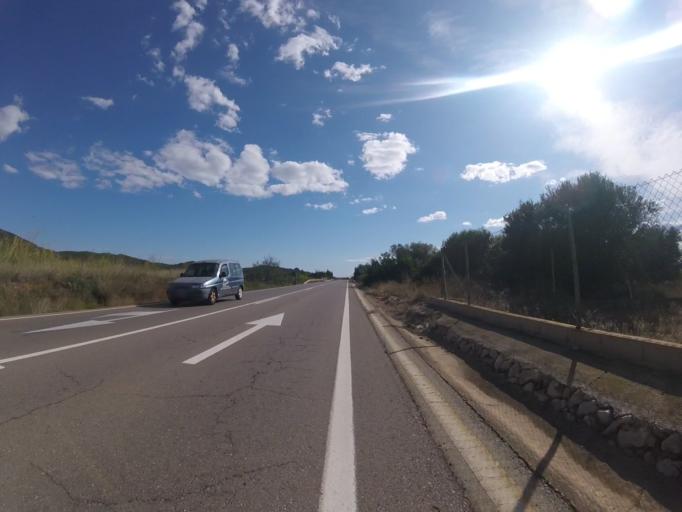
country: ES
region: Valencia
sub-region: Provincia de Castello
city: Alcala de Xivert
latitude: 40.2642
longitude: 0.2425
